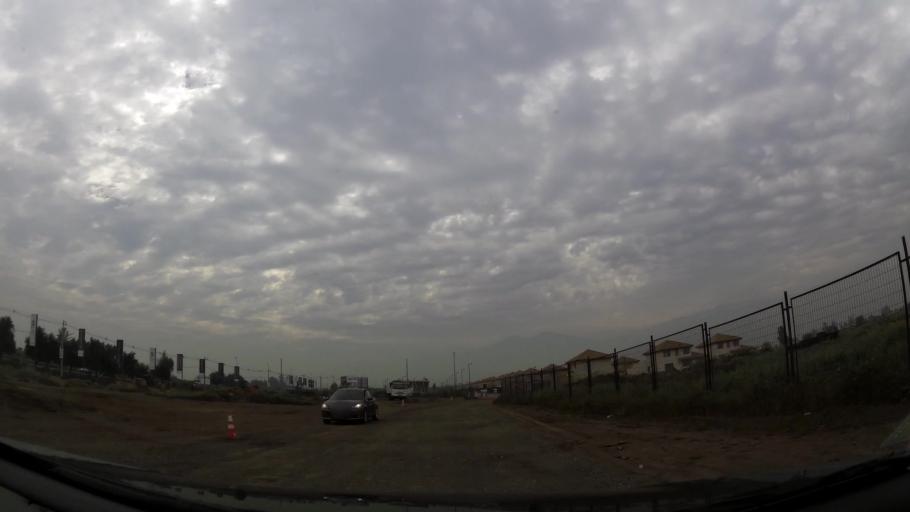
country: CL
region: Santiago Metropolitan
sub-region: Provincia de Chacabuco
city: Chicureo Abajo
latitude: -33.2225
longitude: -70.6788
